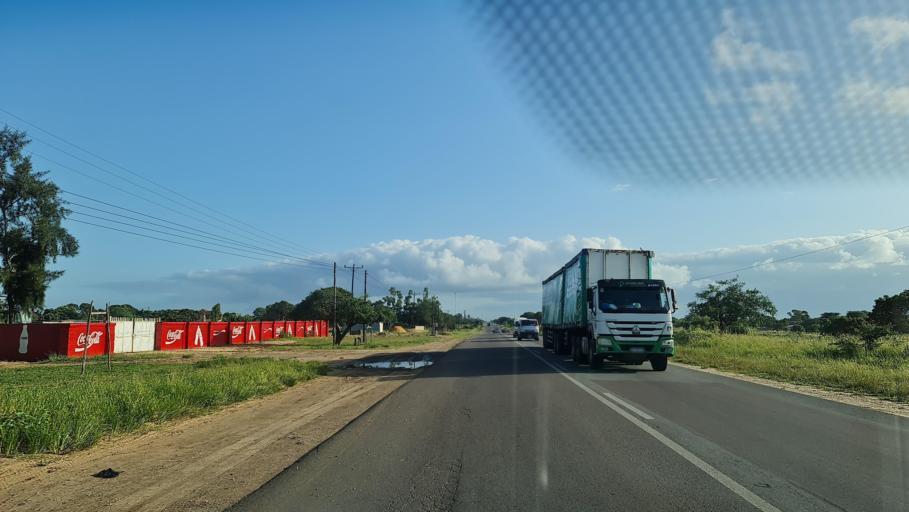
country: MZ
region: Maputo City
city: Maputo
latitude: -25.6804
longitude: 32.6665
